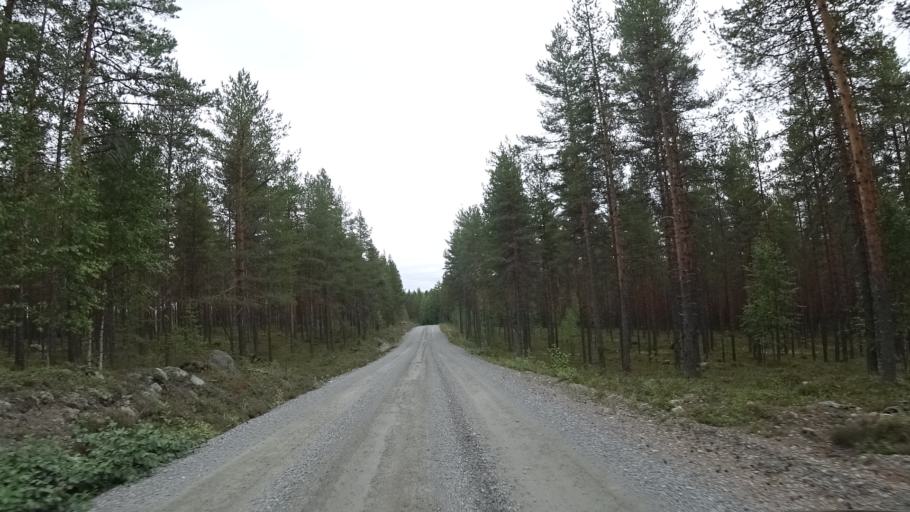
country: FI
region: North Karelia
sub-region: Pielisen Karjala
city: Lieksa
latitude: 63.3713
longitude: 30.3773
